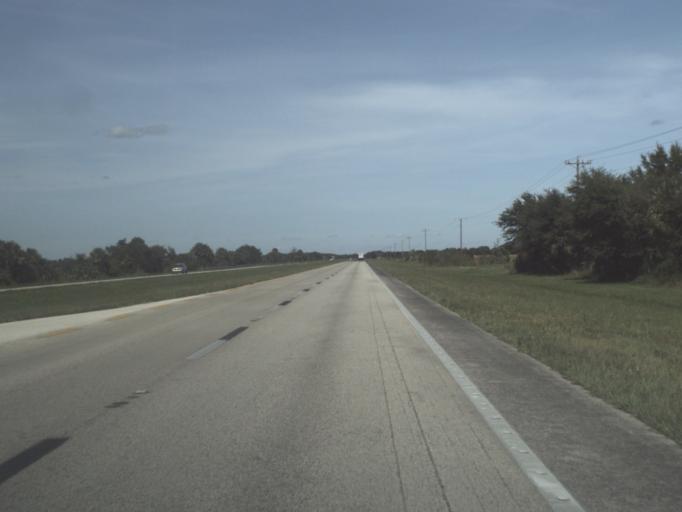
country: US
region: Florida
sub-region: Glades County
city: Moore Haven
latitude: 26.8733
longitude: -81.2214
